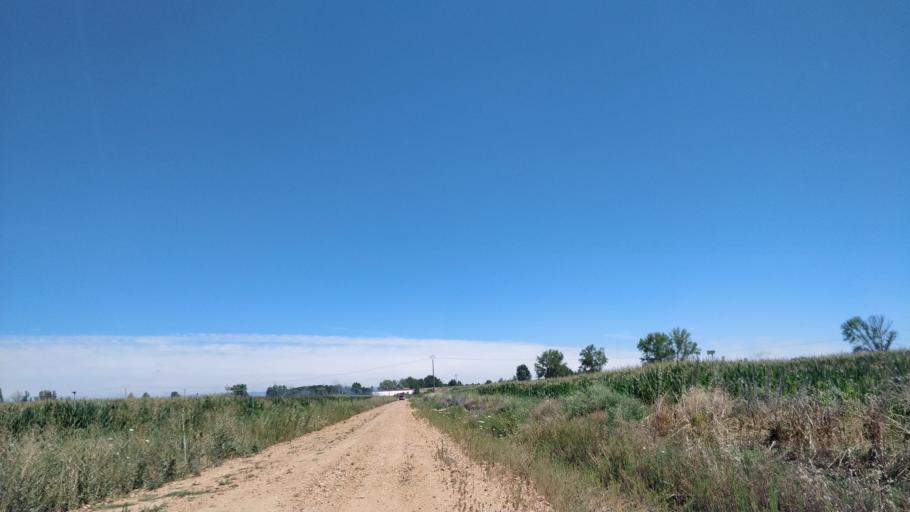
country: ES
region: Castille and Leon
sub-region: Provincia de Leon
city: Bustillo del Paramo
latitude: 42.4729
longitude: -5.8123
